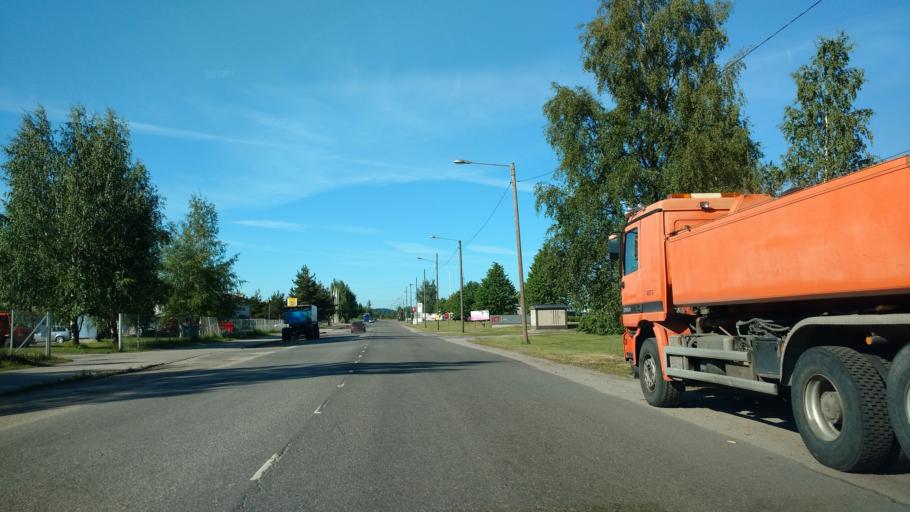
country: FI
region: Varsinais-Suomi
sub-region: Salo
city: Halikko
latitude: 60.3873
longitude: 23.1056
